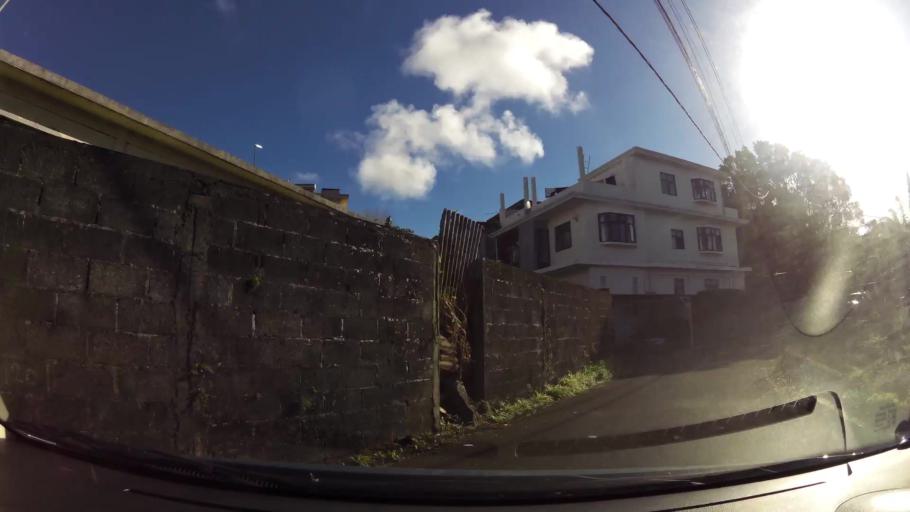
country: MU
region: Plaines Wilhems
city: Curepipe
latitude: -20.3164
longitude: 57.5366
